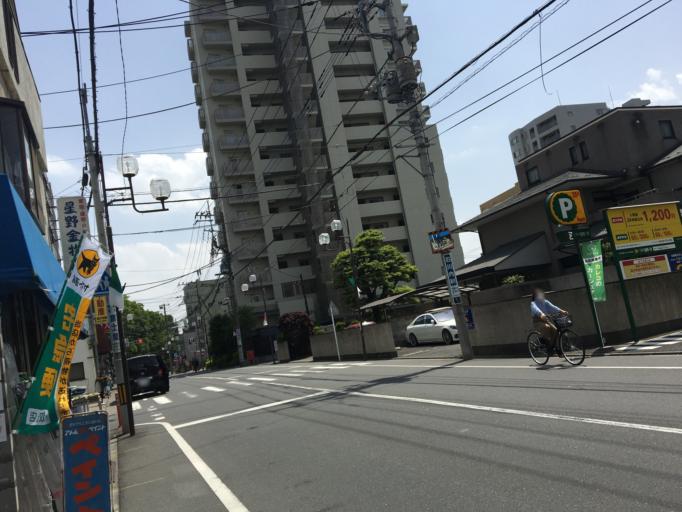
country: JP
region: Saitama
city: Yono
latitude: 35.8549
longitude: 139.6547
